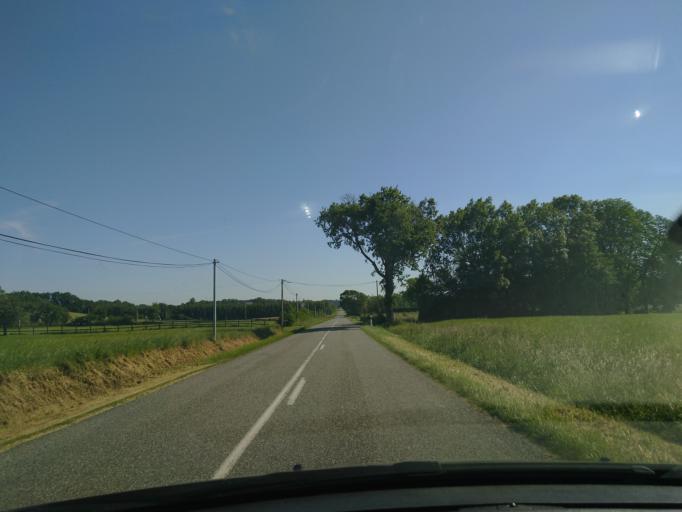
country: FR
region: Midi-Pyrenees
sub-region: Departement du Gers
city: Aubiet
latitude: 43.5471
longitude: 0.7855
